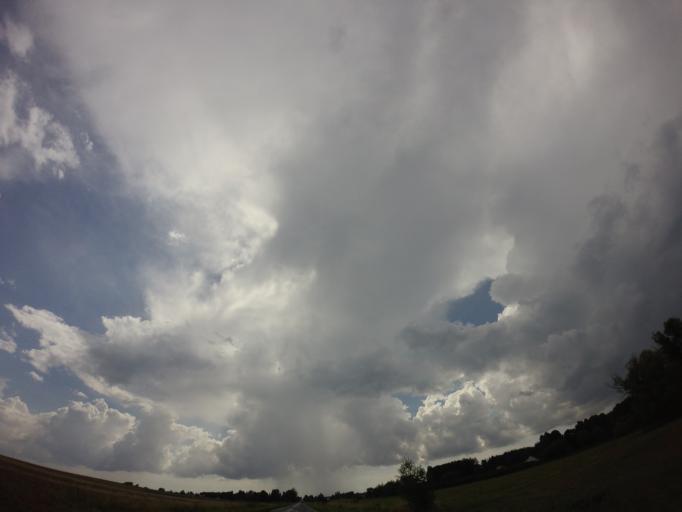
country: PL
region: Swietokrzyskie
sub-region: Powiat staszowski
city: Olesnica
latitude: 50.4667
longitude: 21.0176
